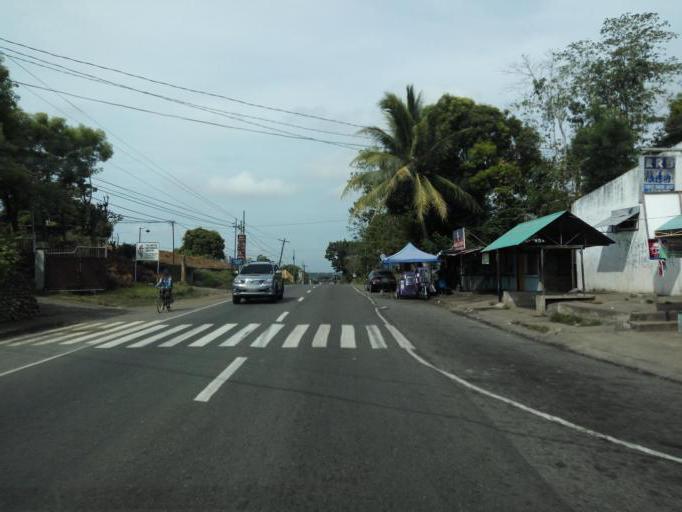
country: PH
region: Cagayan Valley
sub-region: Province of Isabela
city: Naguilian
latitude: 17.0113
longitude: 121.8442
